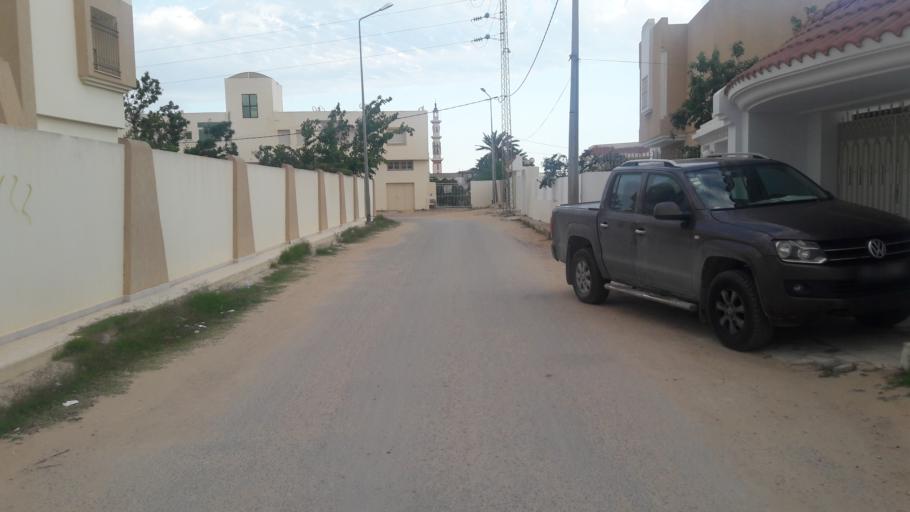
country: TN
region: Safaqis
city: Al Qarmadah
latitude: 34.8102
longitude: 10.7477
